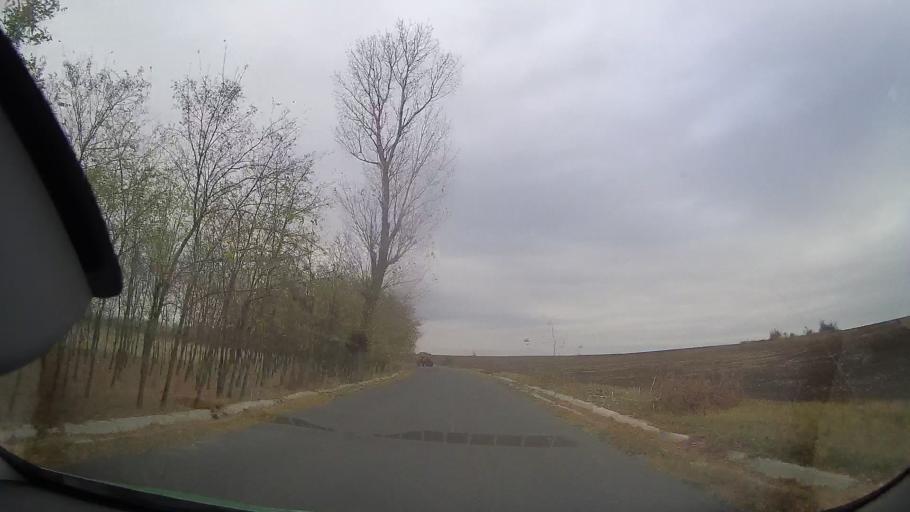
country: RO
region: Braila
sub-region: Comuna Ciocile
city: Ciocile
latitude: 44.7888
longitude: 27.2727
